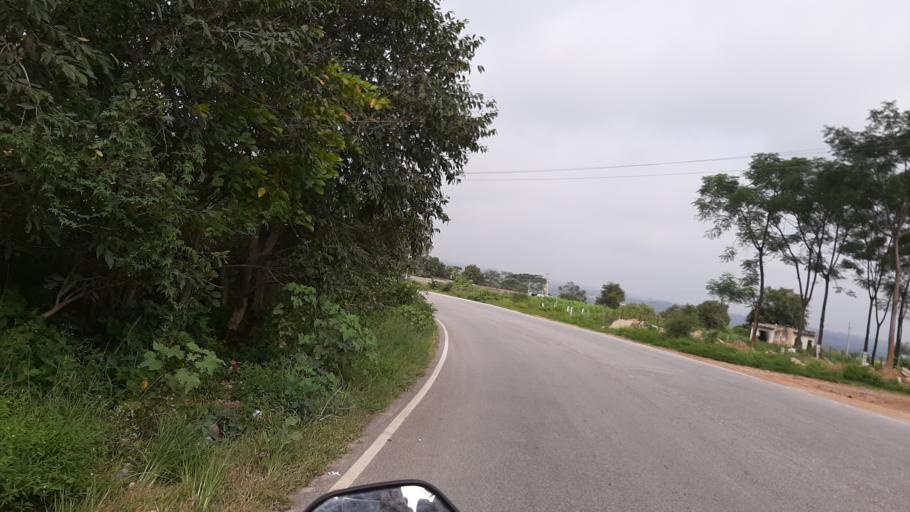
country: IN
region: Karnataka
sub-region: Bangalore Rural
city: Nelamangala
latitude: 12.9742
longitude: 77.3739
